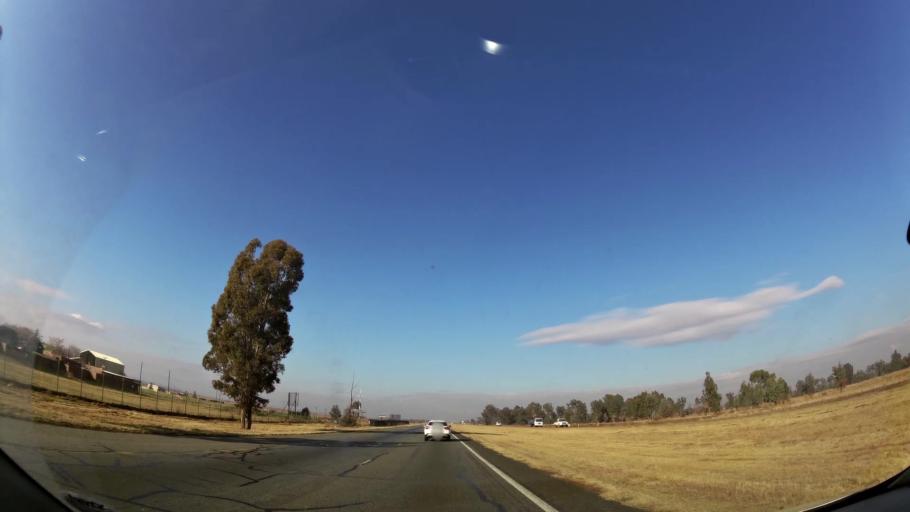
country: ZA
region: Gauteng
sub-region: Sedibeng District Municipality
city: Meyerton
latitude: -26.4368
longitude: 28.0745
